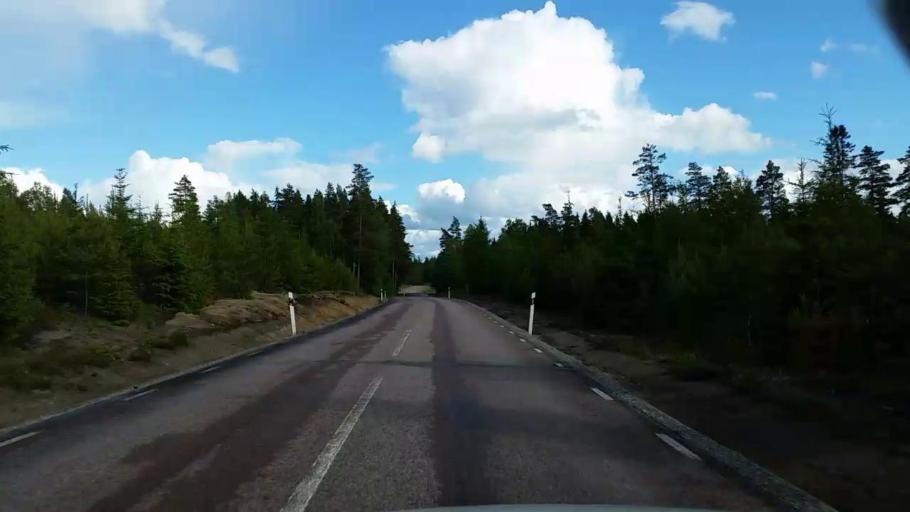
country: SE
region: Vaestmanland
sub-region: Fagersta Kommun
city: Fagersta
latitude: 59.8886
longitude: 15.8269
